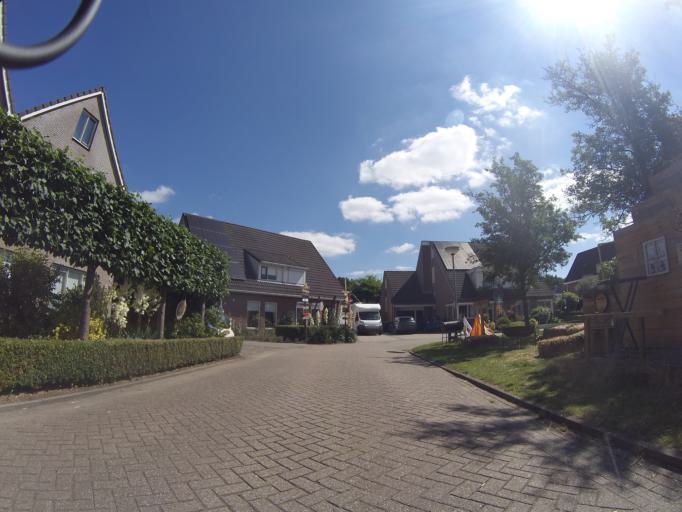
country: NL
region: Drenthe
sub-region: Gemeente Coevorden
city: Sleen
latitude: 52.7652
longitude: 6.8055
